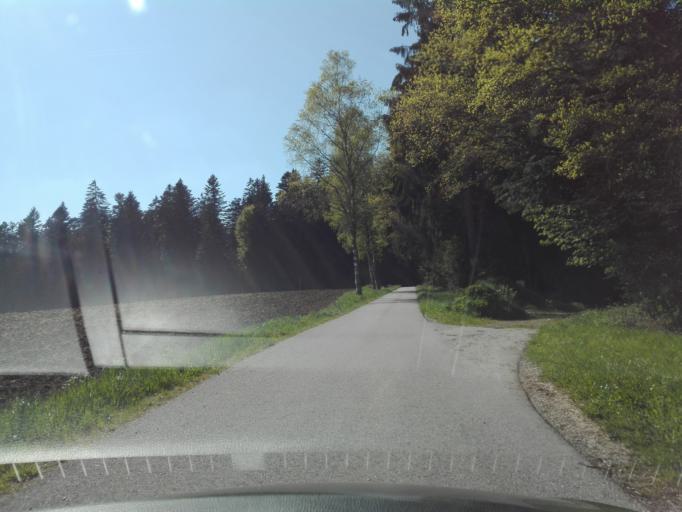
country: AT
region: Upper Austria
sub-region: Politischer Bezirk Rohrbach
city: Pfarrkirchen im Muehlkreis
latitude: 48.4445
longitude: 13.7101
